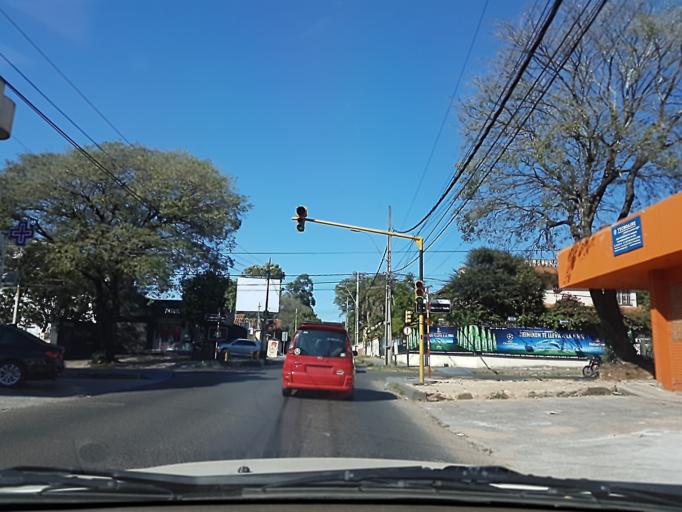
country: PY
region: Asuncion
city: Asuncion
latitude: -25.2988
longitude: -57.5830
